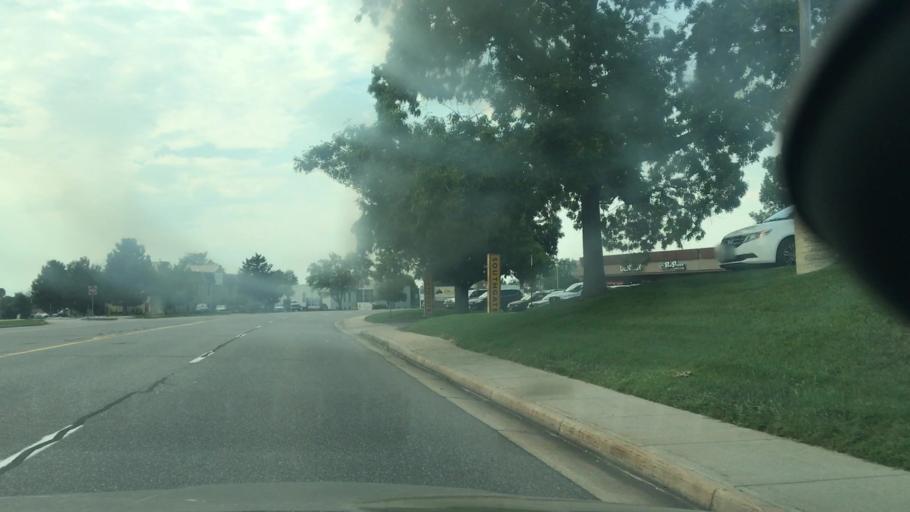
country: US
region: Colorado
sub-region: Arapahoe County
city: Centennial
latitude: 39.5918
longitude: -104.8864
